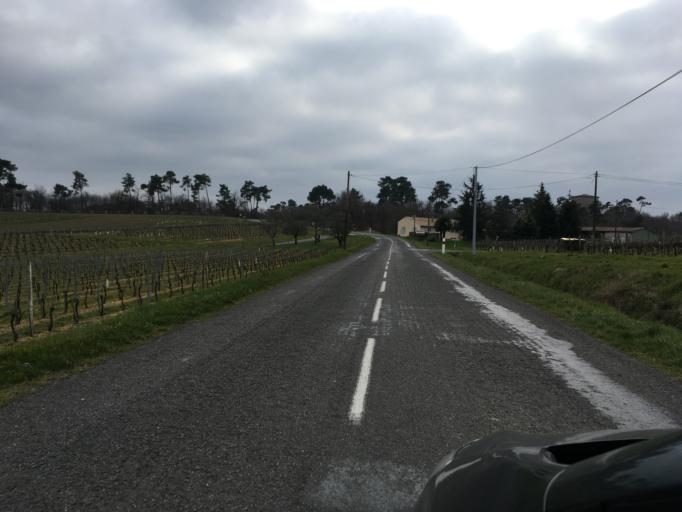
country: FR
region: Aquitaine
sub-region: Departement de la Gironde
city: Saint-Ciers-sur-Gironde
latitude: 45.3227
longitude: -0.5945
